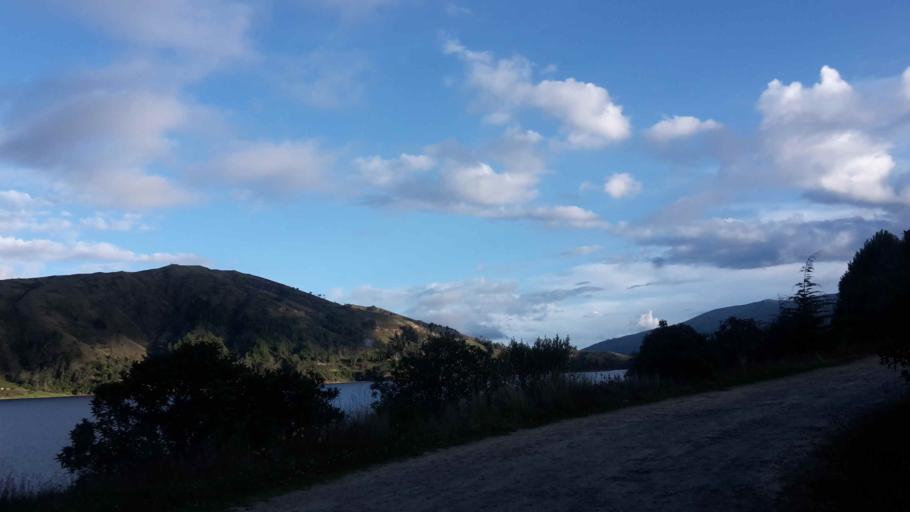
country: BO
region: Cochabamba
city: Colomi
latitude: -17.2705
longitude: -65.9063
